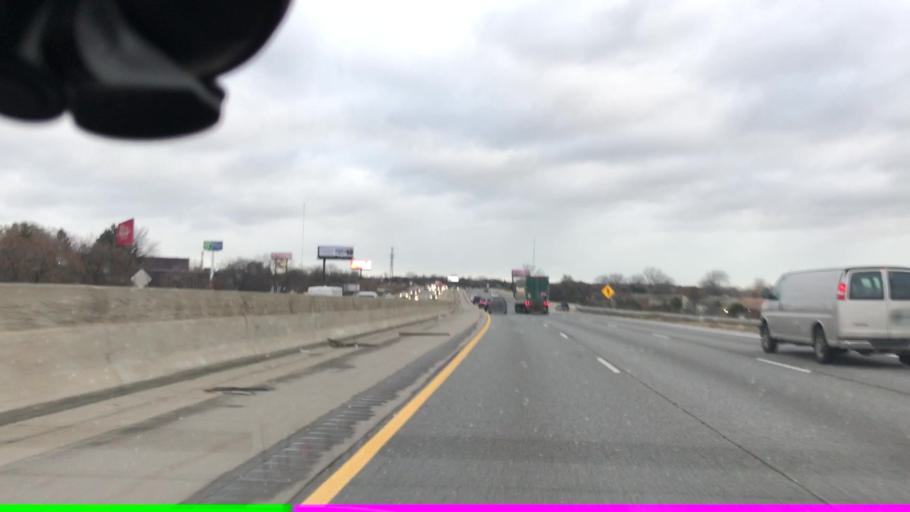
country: US
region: Michigan
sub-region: Macomb County
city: Saint Clair Shores
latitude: 42.5286
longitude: -82.9080
